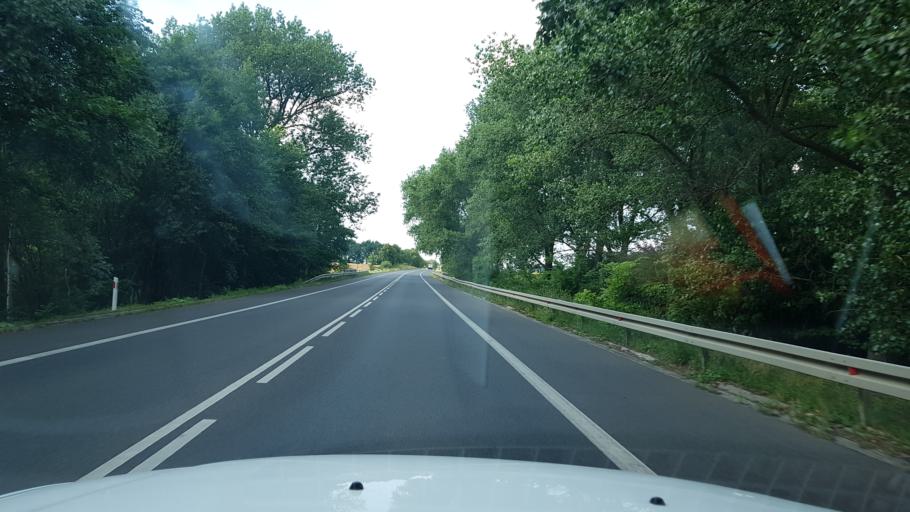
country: PL
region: West Pomeranian Voivodeship
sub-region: Powiat gryfinski
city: Stare Czarnowo
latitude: 53.2193
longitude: 14.7977
